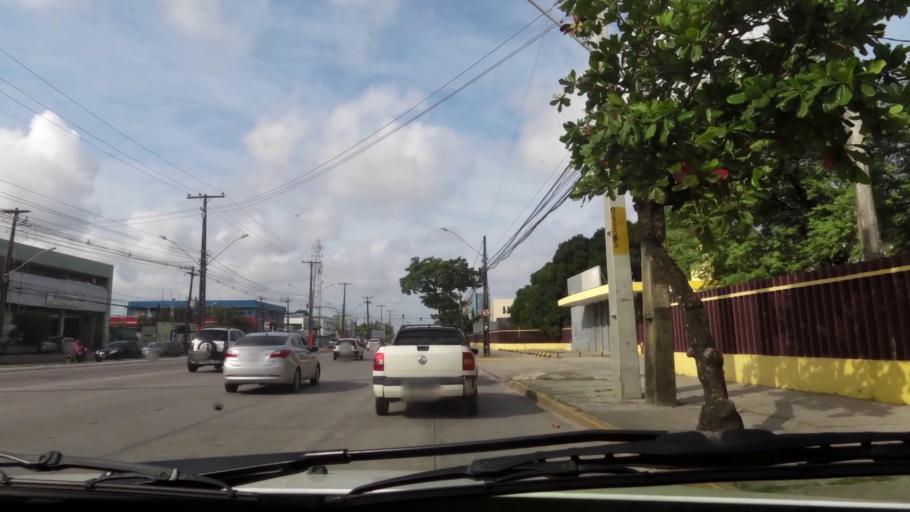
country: BR
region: Pernambuco
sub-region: Recife
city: Recife
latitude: -8.0946
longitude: -34.9092
